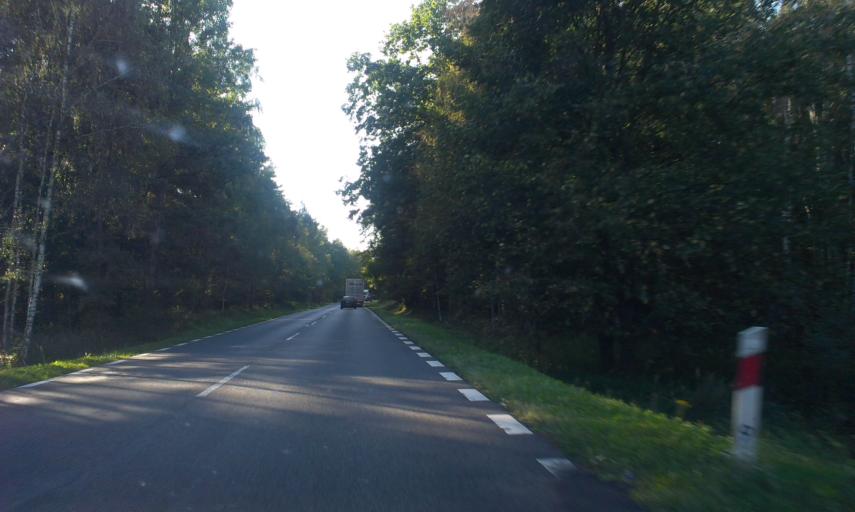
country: PL
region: Kujawsko-Pomorskie
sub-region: Powiat swiecki
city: Swiekatowo
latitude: 53.4896
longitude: 18.0999
